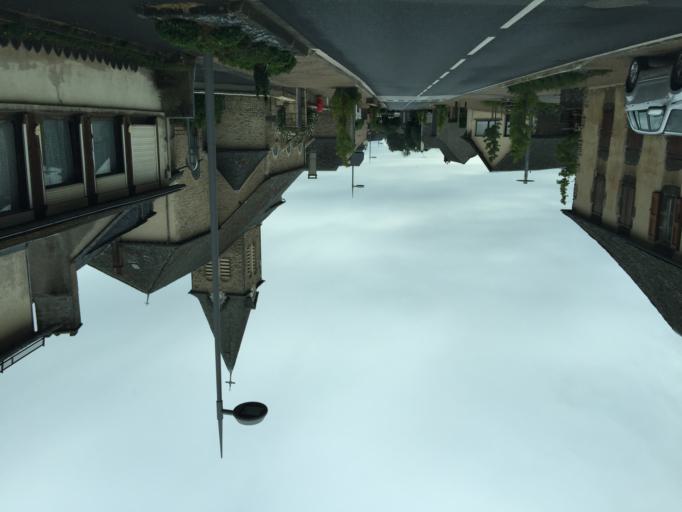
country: FR
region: Midi-Pyrenees
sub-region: Departement de l'Aveyron
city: Espalion
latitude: 44.5882
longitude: 2.7925
